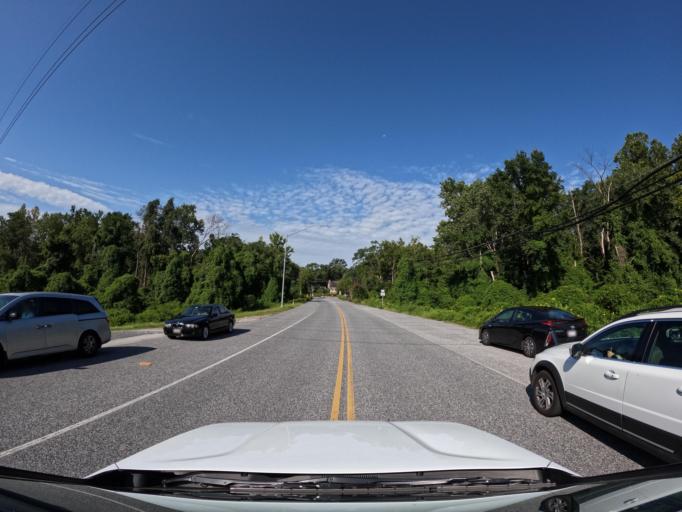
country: US
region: Maryland
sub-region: Baltimore County
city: Mays Chapel
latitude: 39.4012
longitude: -76.6650
